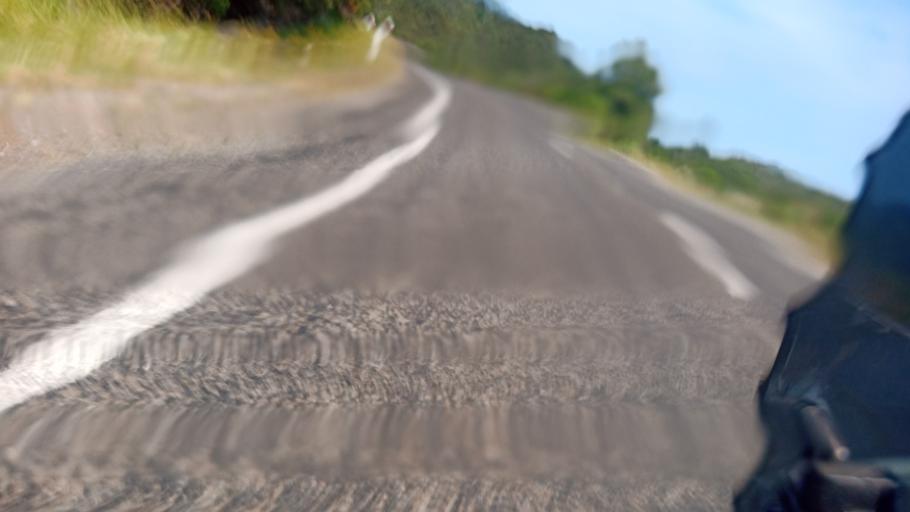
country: NZ
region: Bay of Plenty
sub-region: Opotiki District
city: Opotiki
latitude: -37.5906
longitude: 178.2303
